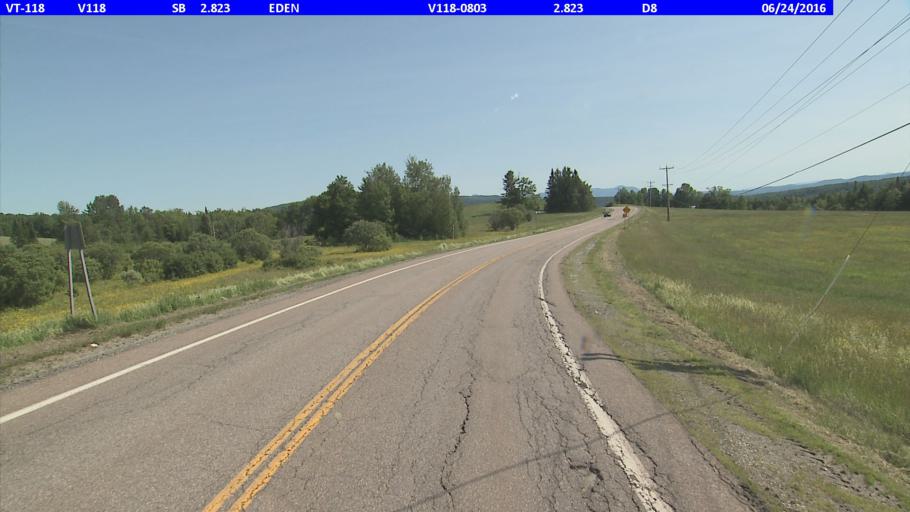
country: US
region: Vermont
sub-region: Lamoille County
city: Johnson
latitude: 44.7435
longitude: -72.5662
